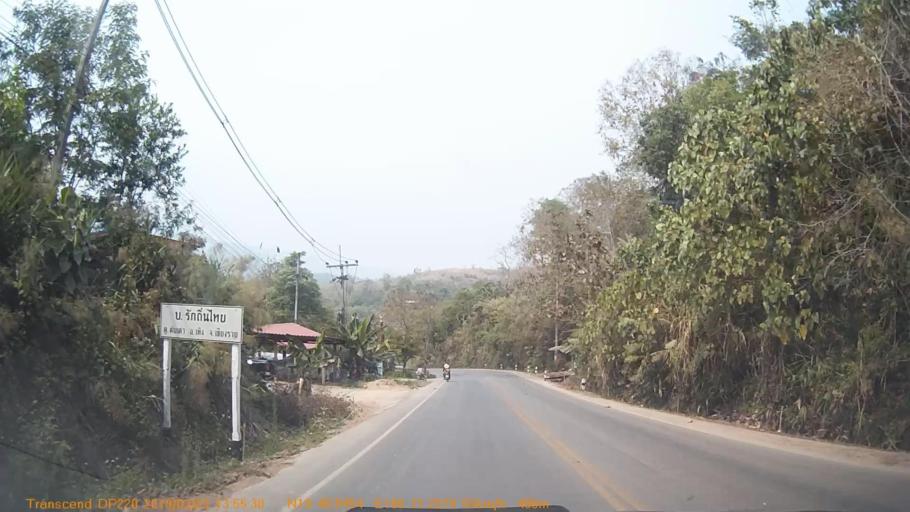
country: TH
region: Chiang Rai
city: Khun Tan
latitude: 19.8009
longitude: 100.3543
